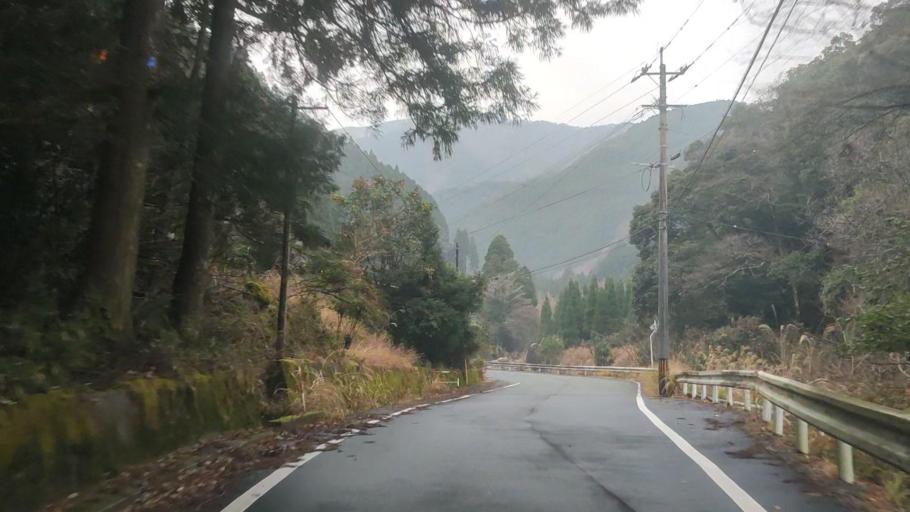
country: JP
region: Kumamoto
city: Matsubase
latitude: 32.5990
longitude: 130.8902
